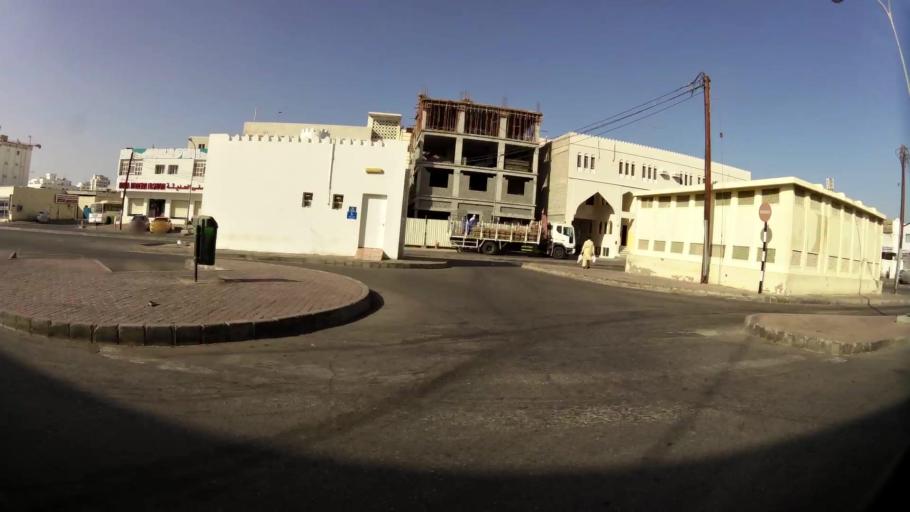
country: OM
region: Muhafazat Masqat
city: Muscat
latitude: 23.5909
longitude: 58.5470
